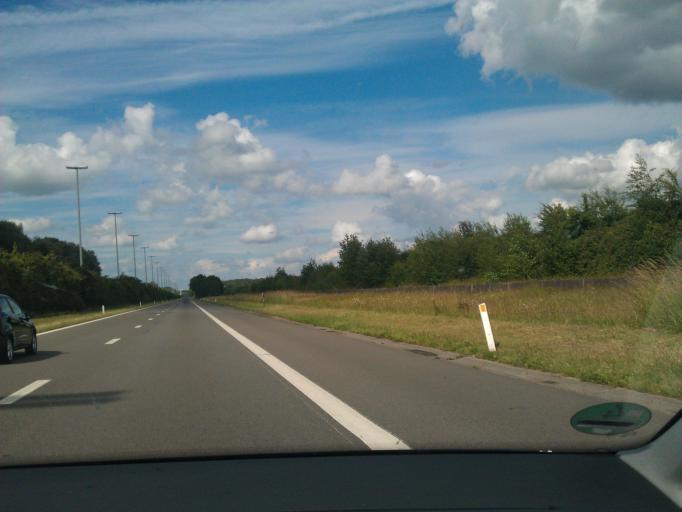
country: BE
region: Wallonia
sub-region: Province de Liege
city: Lontzen
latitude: 50.6710
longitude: 6.0334
